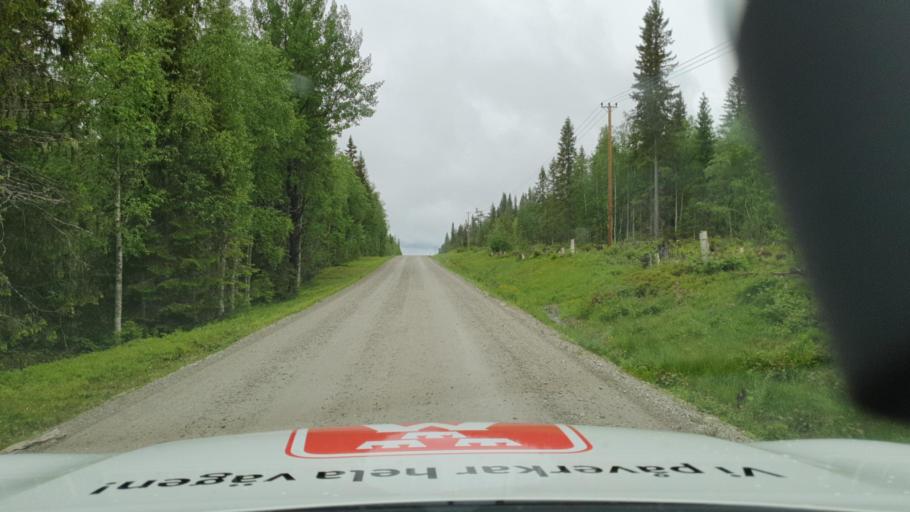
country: SE
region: Vaesterbotten
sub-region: Asele Kommun
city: Asele
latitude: 63.9734
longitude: 16.8587
